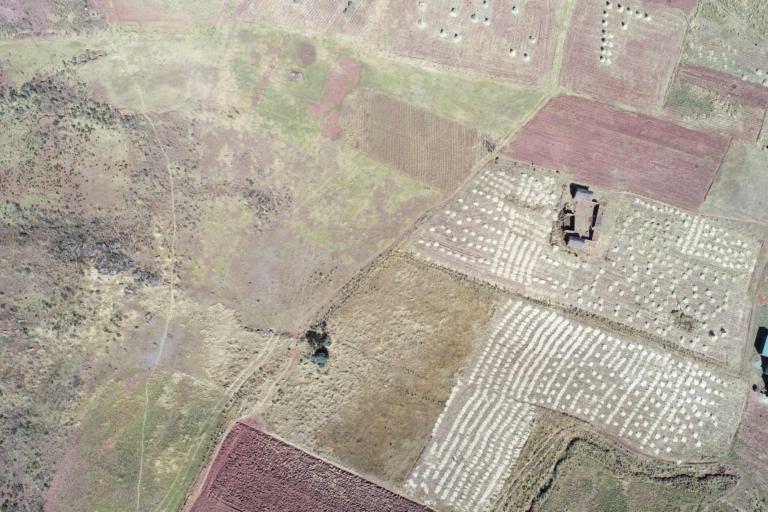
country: BO
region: La Paz
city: Tiahuanaco
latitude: -16.5959
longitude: -68.7616
